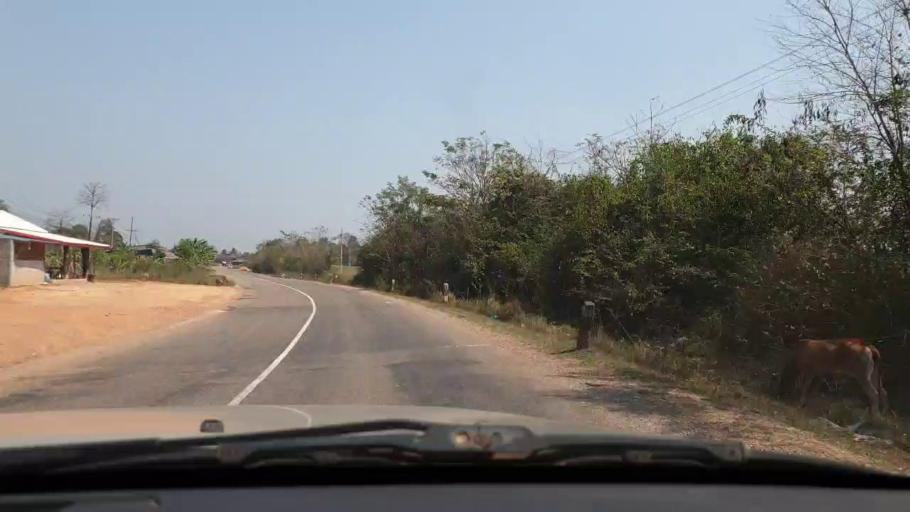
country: TH
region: Nong Khai
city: Rattanawapi
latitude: 18.2177
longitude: 103.0975
